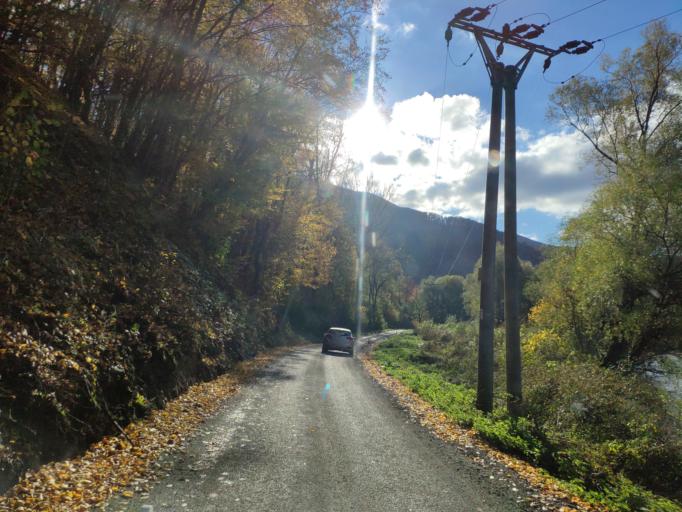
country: SK
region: Presovsky
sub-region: Okres Presov
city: Presov
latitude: 48.8565
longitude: 21.1863
